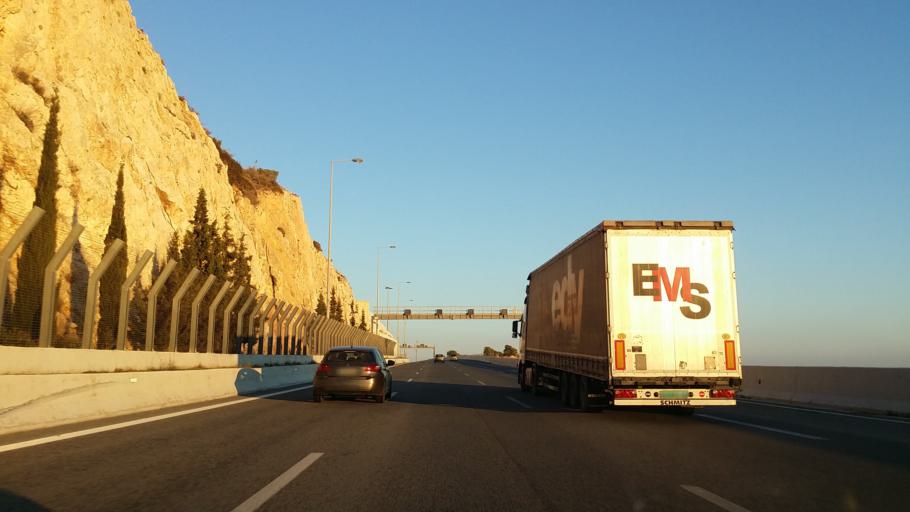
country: GR
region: Attica
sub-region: Nomarchia Dytikis Attikis
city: Megara
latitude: 37.9729
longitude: 23.2985
